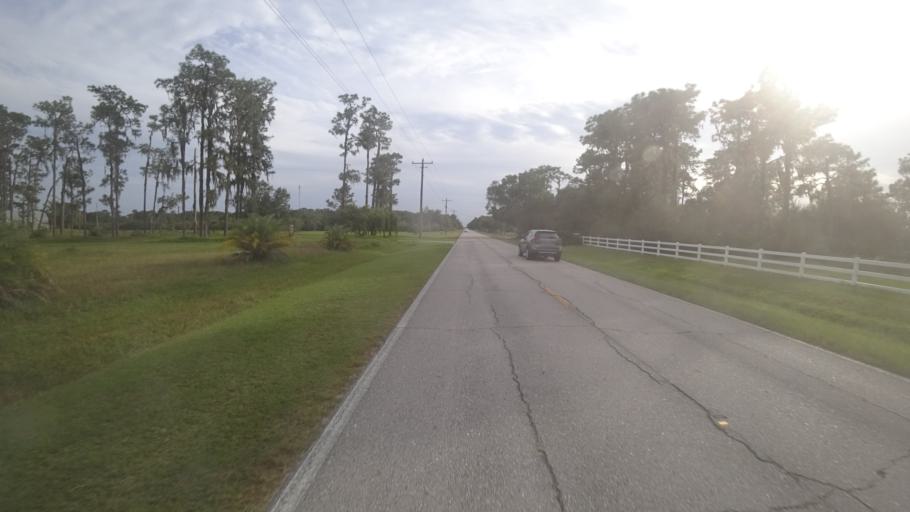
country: US
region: Florida
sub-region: Sarasota County
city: The Meadows
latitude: 27.4190
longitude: -82.2709
